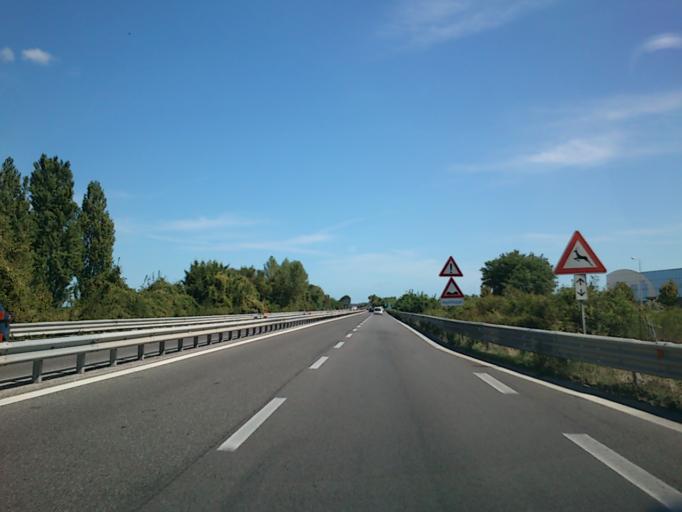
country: IT
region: The Marches
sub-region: Provincia di Pesaro e Urbino
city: Lucrezia
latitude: 43.7696
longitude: 12.9595
